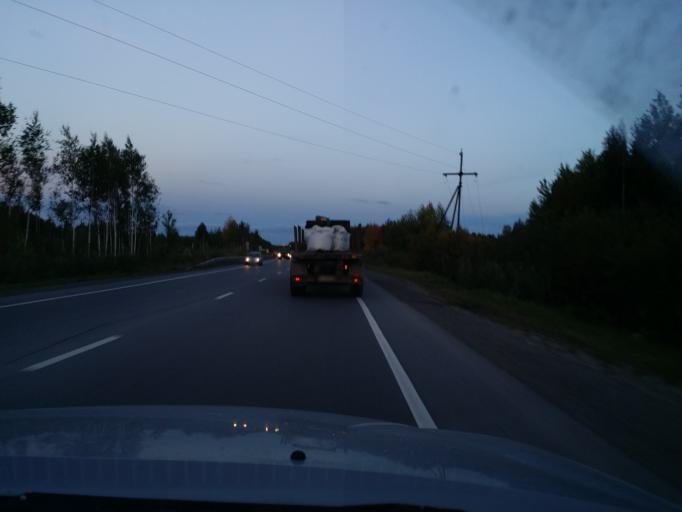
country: RU
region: Khanty-Mansiyskiy Avtonomnyy Okrug
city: Nizhnevartovsk
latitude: 61.0233
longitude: 76.3715
